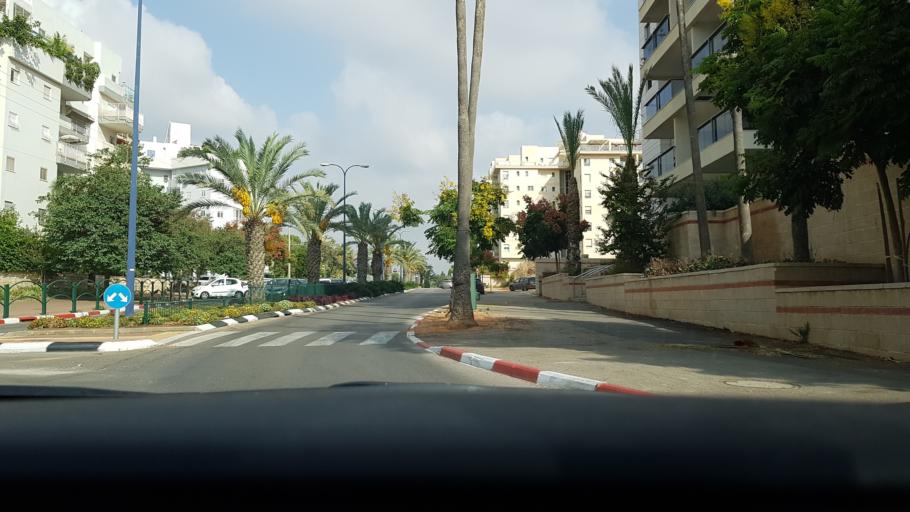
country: IL
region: Central District
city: Ness Ziona
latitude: 31.9009
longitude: 34.8196
